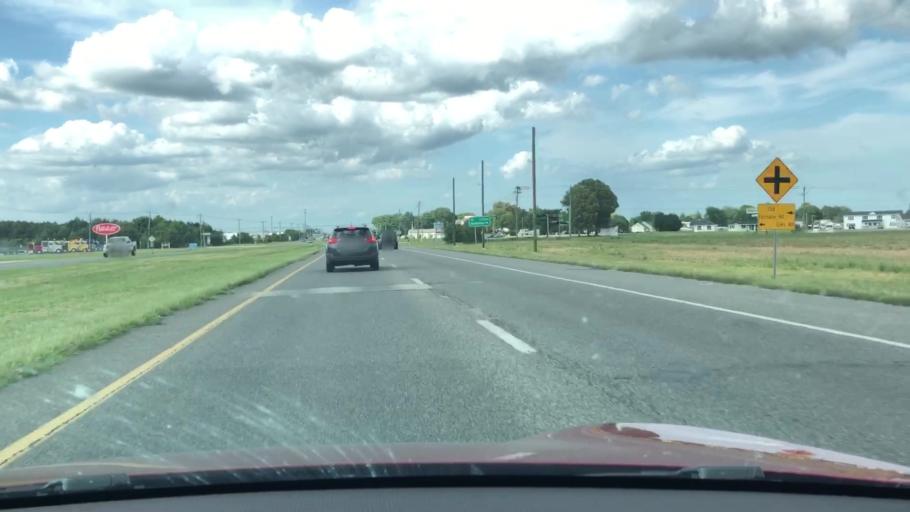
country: US
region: Delaware
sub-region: Sussex County
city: Seaford
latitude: 38.6830
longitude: -75.5912
